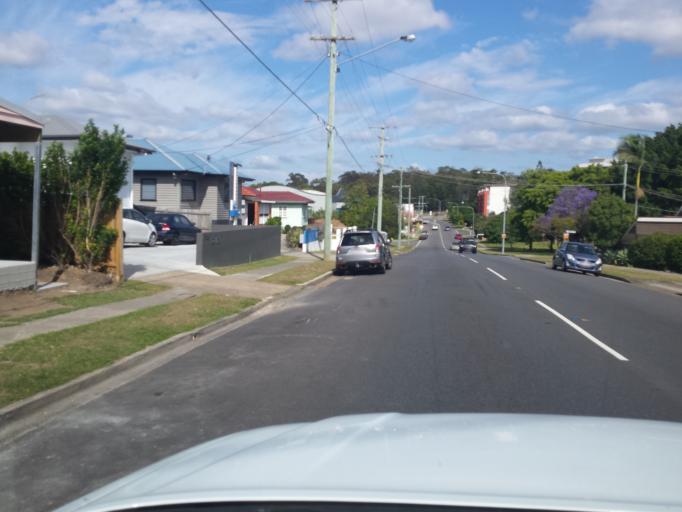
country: AU
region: Queensland
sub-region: Brisbane
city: Chermside West
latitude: -27.3929
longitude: 153.0270
